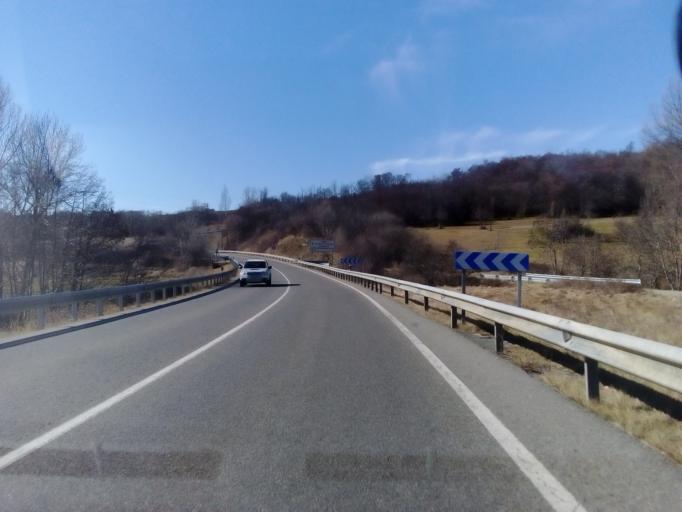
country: ES
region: Catalonia
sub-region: Provincia de Girona
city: Bolvir
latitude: 42.4181
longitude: 1.8620
